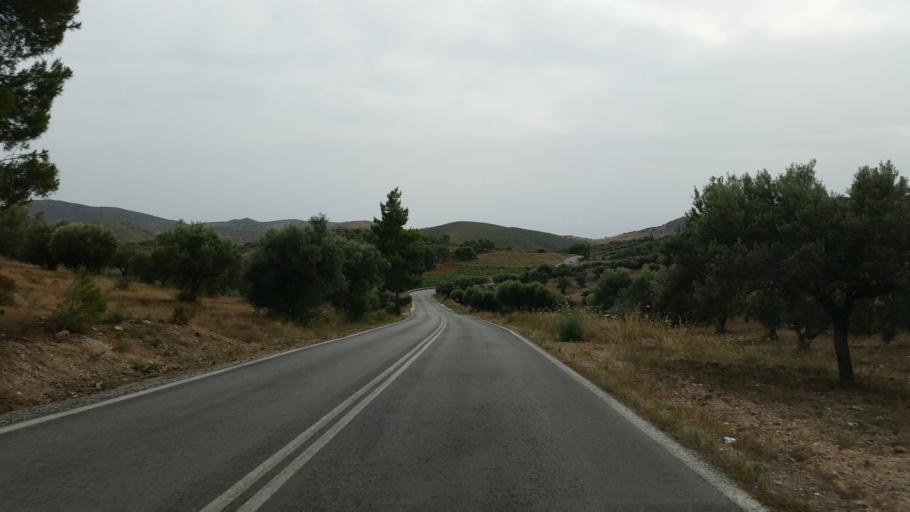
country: GR
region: Attica
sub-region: Nomarchia Anatolikis Attikis
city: Lavrio
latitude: 37.7212
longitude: 24.0037
